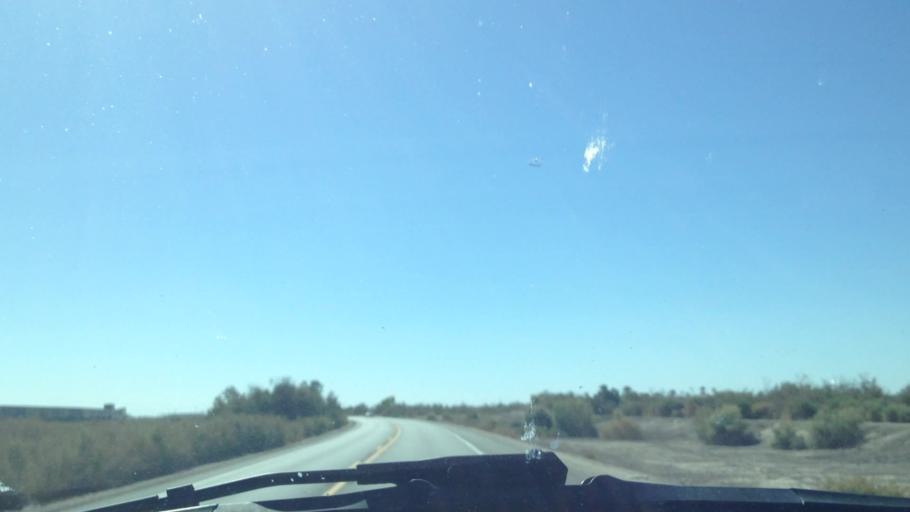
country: US
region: California
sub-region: Riverside County
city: Mecca
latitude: 33.5596
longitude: -116.0696
